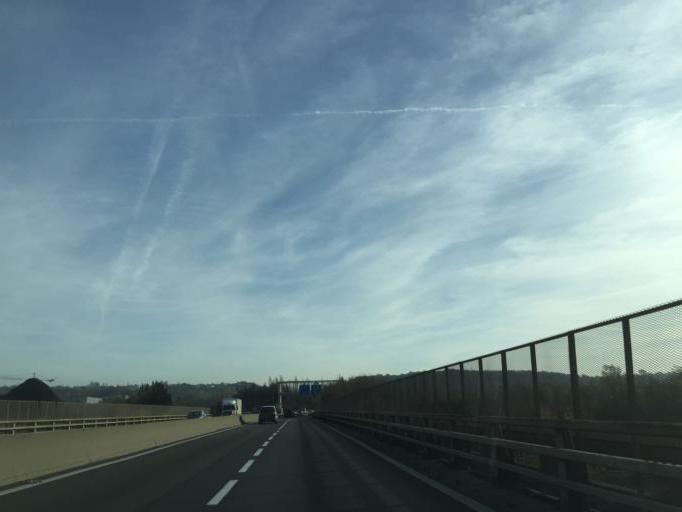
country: FR
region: Rhone-Alpes
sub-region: Departement de l'Isere
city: Chasse-sur-Rhone
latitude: 45.5883
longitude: 4.7921
